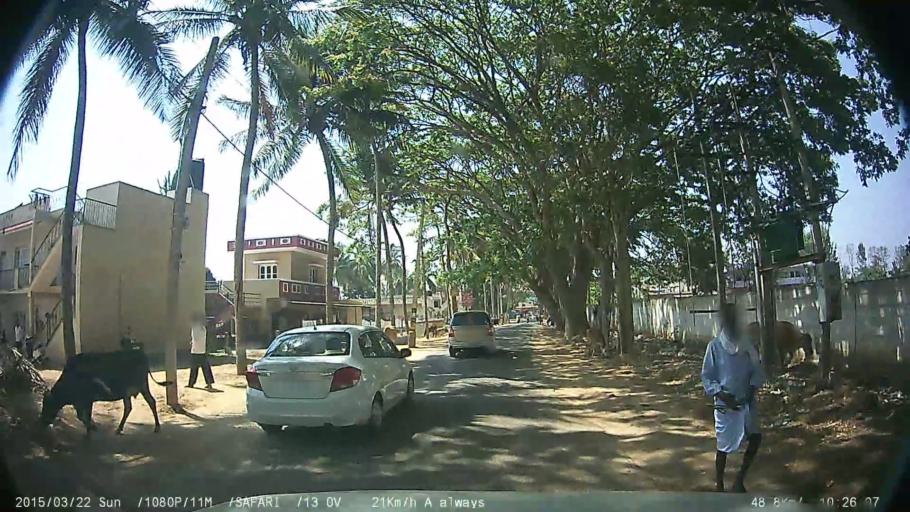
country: IN
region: Karnataka
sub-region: Bangalore Urban
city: Anekal
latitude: 12.8078
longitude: 77.5787
